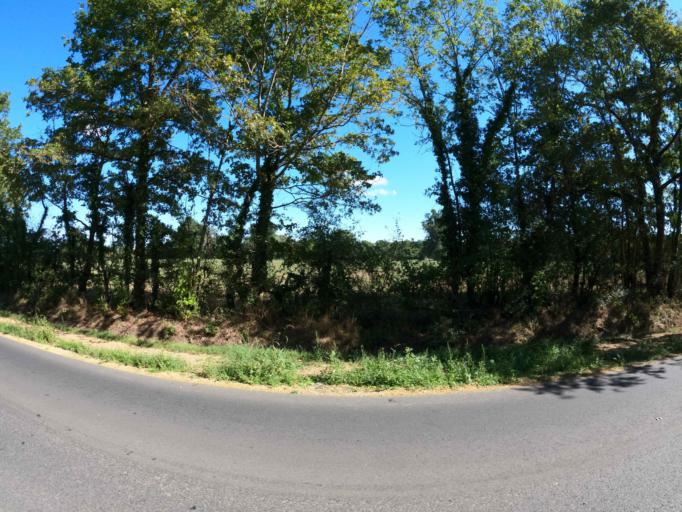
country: FR
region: Poitou-Charentes
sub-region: Departement de la Vienne
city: Saulge
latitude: 46.4017
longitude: 0.8951
